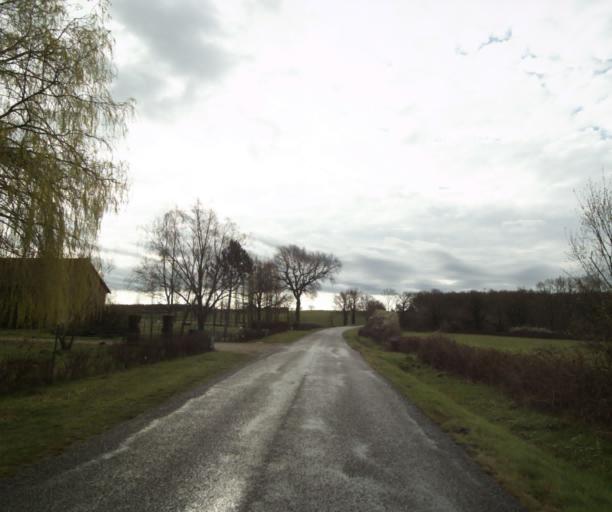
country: FR
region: Auvergne
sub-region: Departement de l'Allier
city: Toulon-sur-Allier
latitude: 46.5339
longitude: 3.4031
